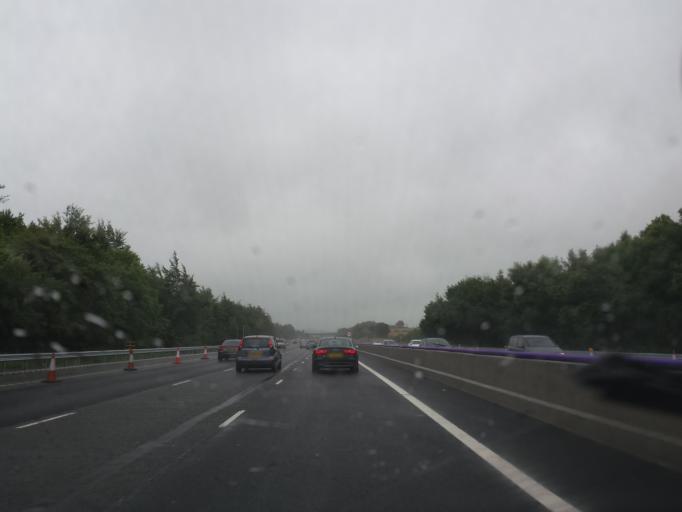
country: GB
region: England
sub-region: Derbyshire
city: Tibshelf
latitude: 53.1719
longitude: -1.3247
